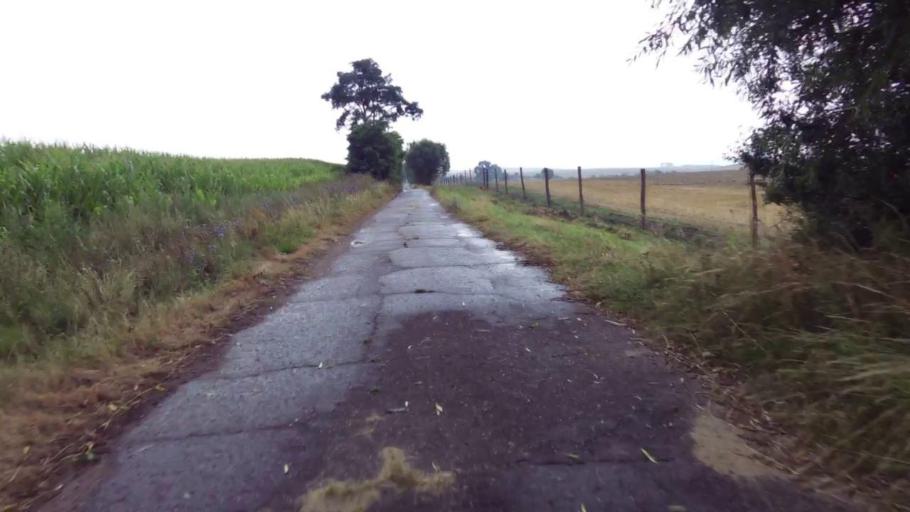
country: PL
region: West Pomeranian Voivodeship
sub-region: Powiat choszczenski
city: Recz
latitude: 53.2630
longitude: 15.4613
